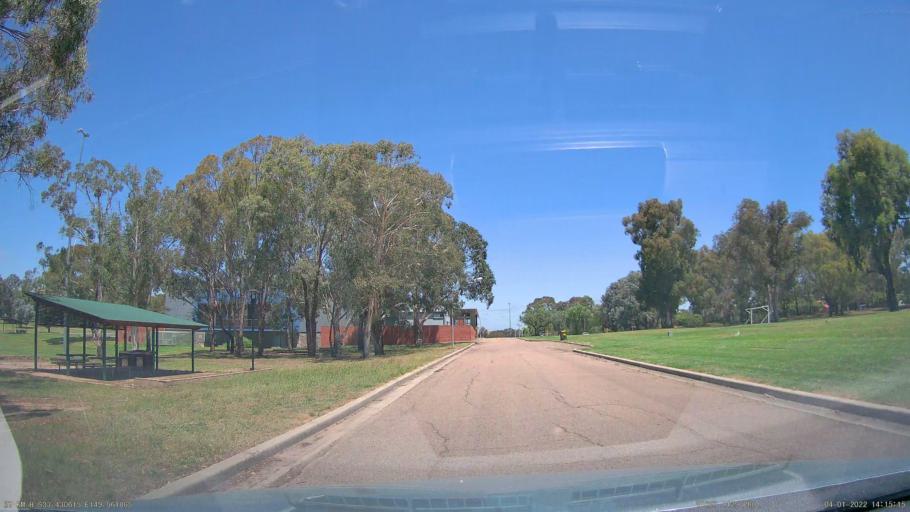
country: AU
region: New South Wales
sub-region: Bathurst Regional
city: Bathurst
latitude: -33.4309
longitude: 149.5620
